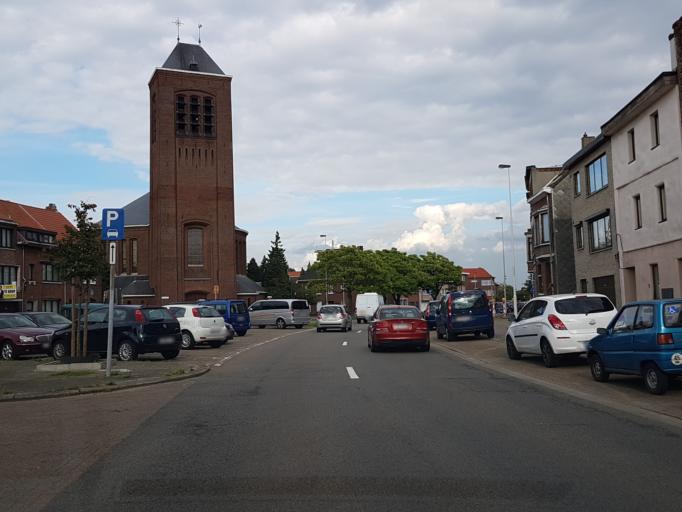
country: BE
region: Flanders
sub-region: Provincie Antwerpen
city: Antwerpen
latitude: 51.2553
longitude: 4.4431
